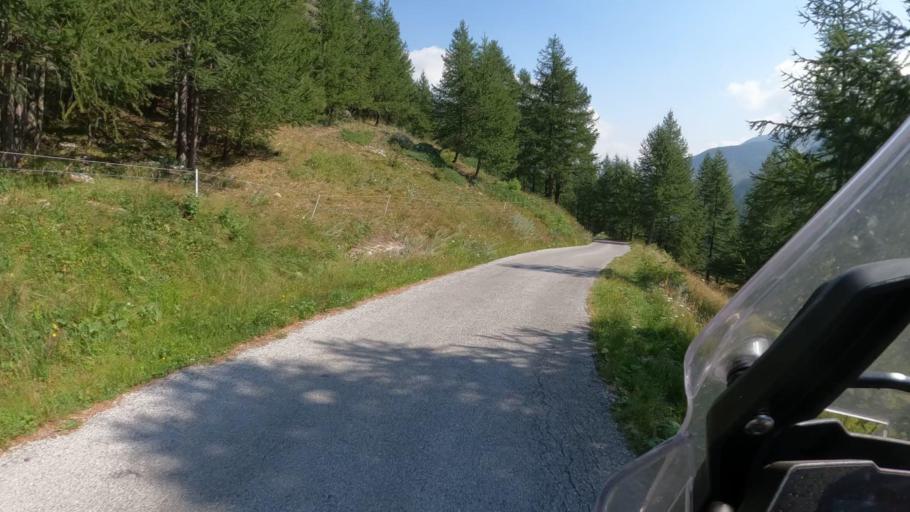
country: IT
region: Piedmont
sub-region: Provincia di Cuneo
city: Canosio
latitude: 44.4132
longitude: 7.0405
